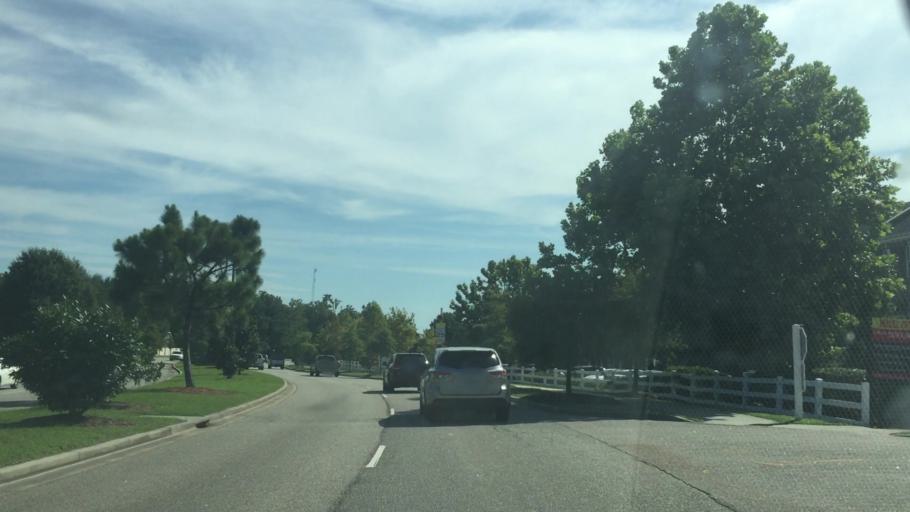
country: US
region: South Carolina
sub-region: Horry County
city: Myrtle Beach
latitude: 33.7232
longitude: -78.8671
